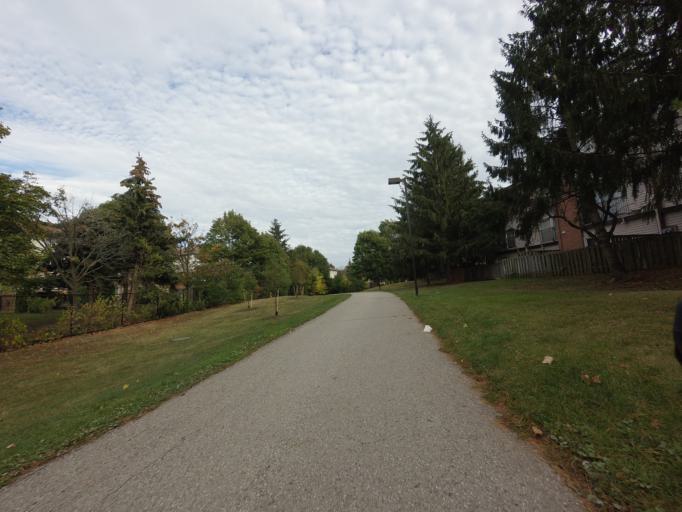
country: CA
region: Ontario
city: Mississauga
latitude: 43.5390
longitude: -79.6859
